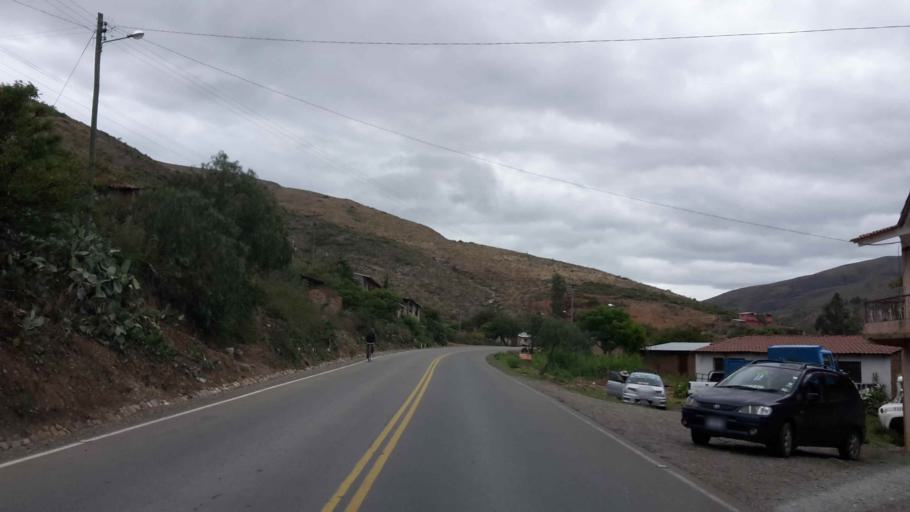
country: BO
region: Cochabamba
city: Punata
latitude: -17.5144
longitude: -65.8173
